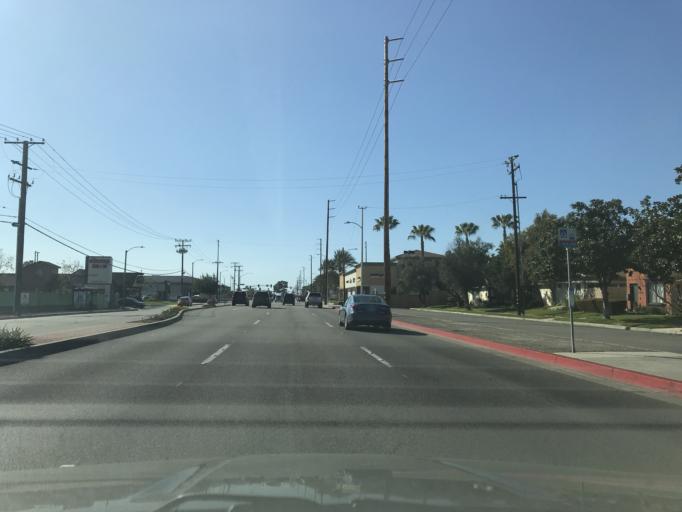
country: US
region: California
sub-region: Orange County
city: Fountain Valley
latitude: 33.6724
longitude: -117.9509
